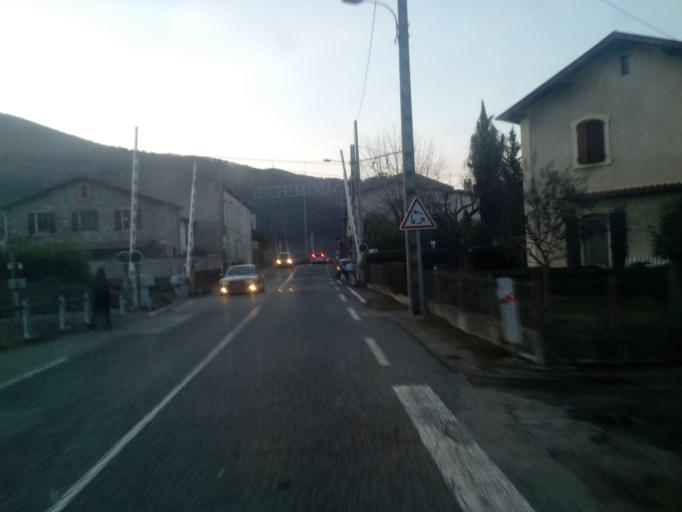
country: FR
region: Midi-Pyrenees
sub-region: Departement de l'Ariege
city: Saint-Paul-de-Jarrat
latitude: 42.9180
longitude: 1.6419
